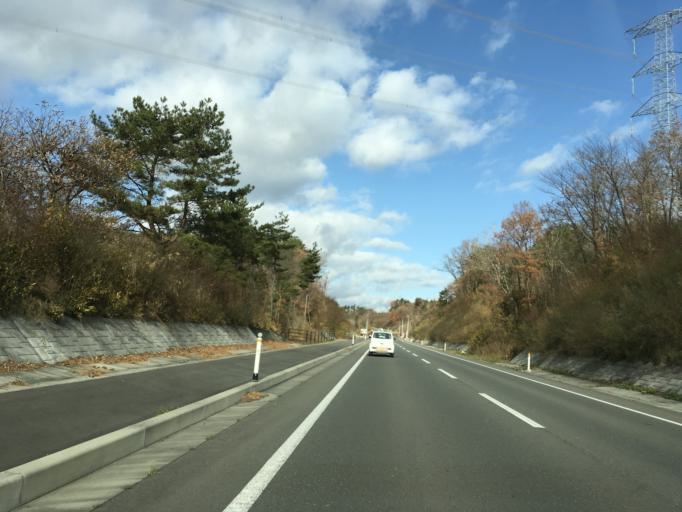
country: JP
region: Iwate
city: Ichinoseki
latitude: 38.8710
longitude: 141.1604
